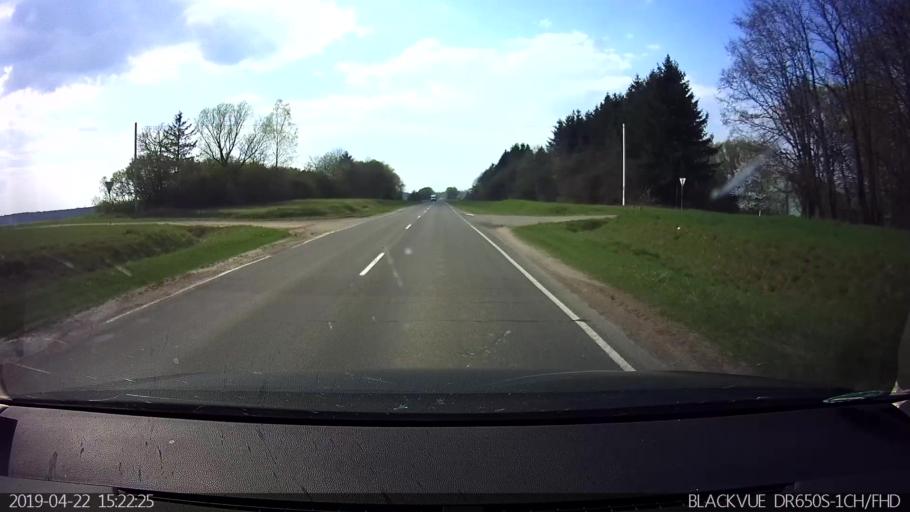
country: BY
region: Brest
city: Vysokaye
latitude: 52.3498
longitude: 23.4466
